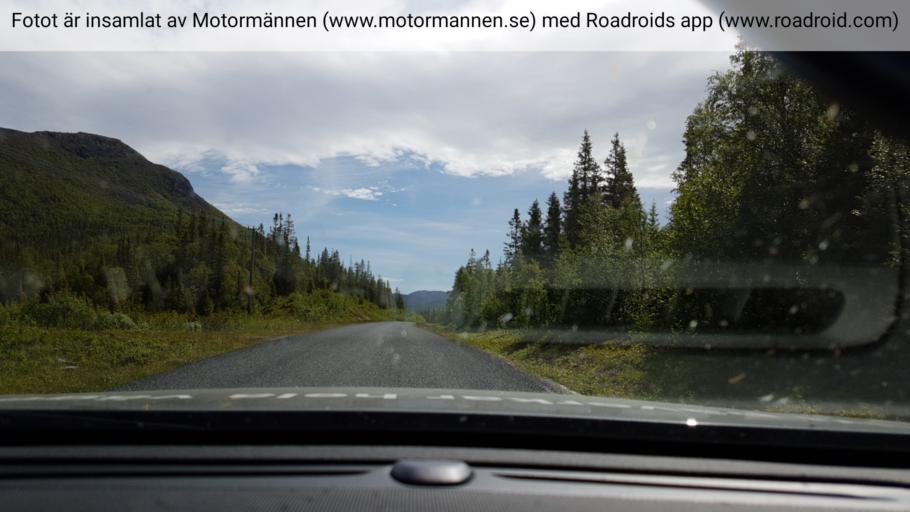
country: SE
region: Vaesterbotten
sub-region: Vilhelmina Kommun
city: Sjoberg
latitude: 65.2471
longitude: 15.4240
